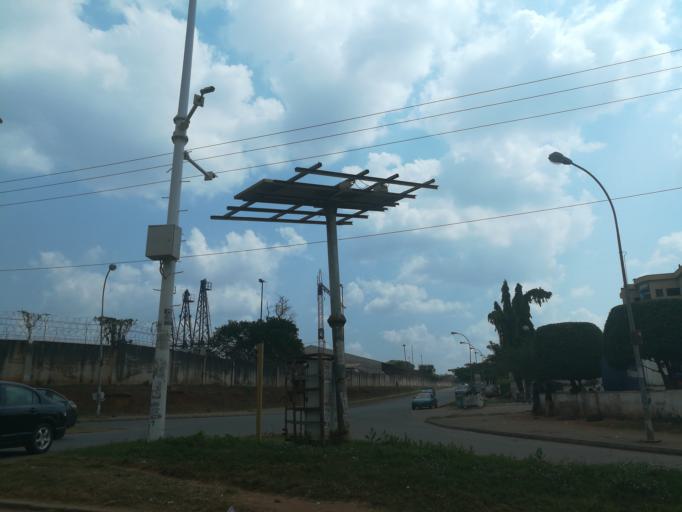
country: NG
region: Abuja Federal Capital Territory
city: Abuja
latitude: 9.0613
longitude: 7.4455
